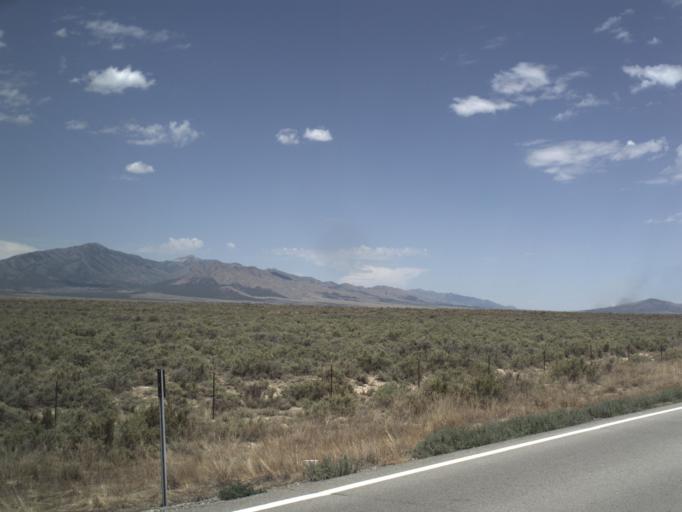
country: US
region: Utah
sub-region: Tooele County
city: Tooele
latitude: 40.2450
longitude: -112.4005
